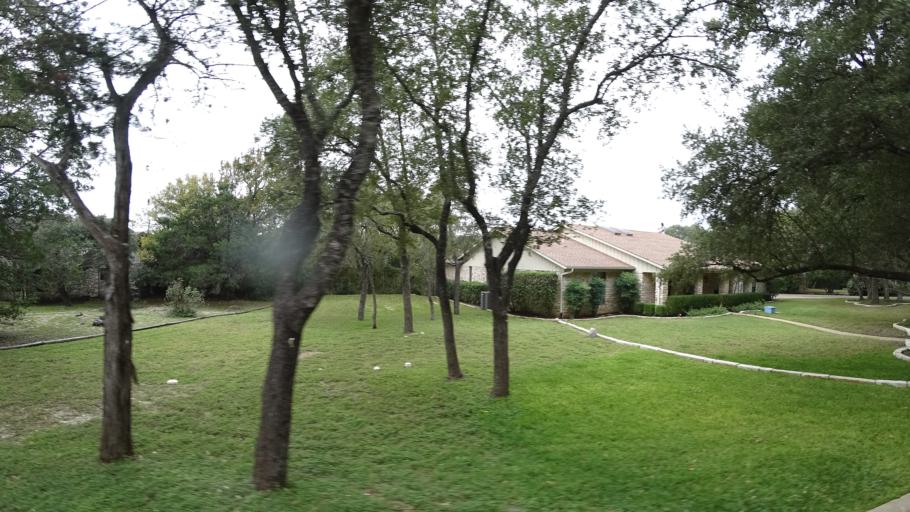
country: US
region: Texas
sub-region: Williamson County
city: Anderson Mill
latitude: 30.4428
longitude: -97.8177
